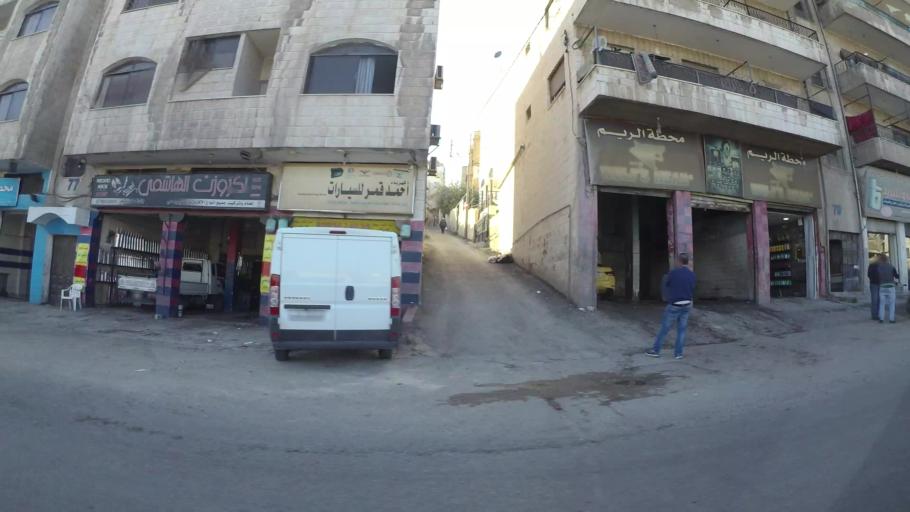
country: JO
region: Amman
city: Amman
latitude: 31.9664
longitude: 35.9600
